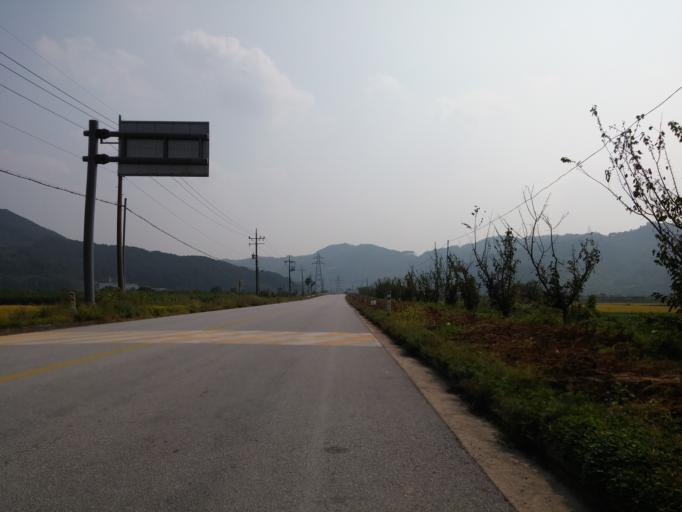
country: KR
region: Chungcheongbuk-do
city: Yong-dong
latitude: 36.3223
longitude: 127.7588
